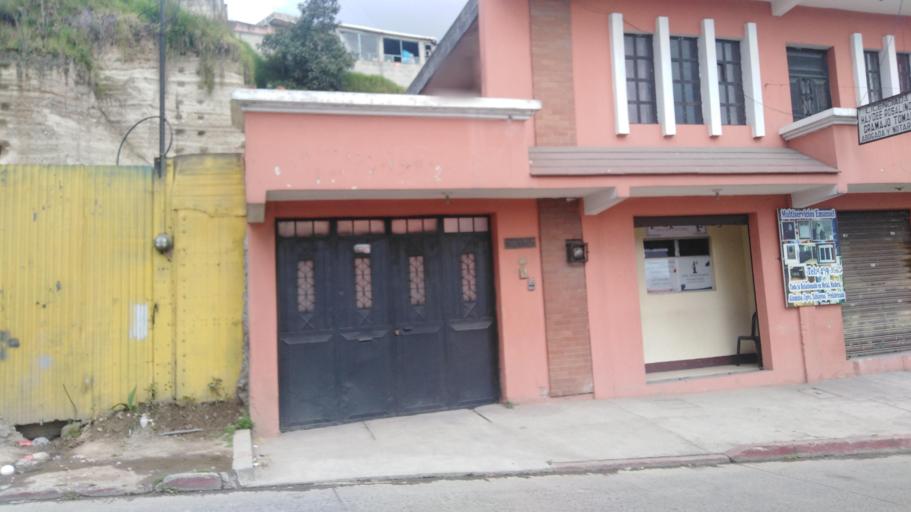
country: GT
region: Quetzaltenango
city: Quetzaltenango
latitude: 14.8523
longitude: -91.5123
